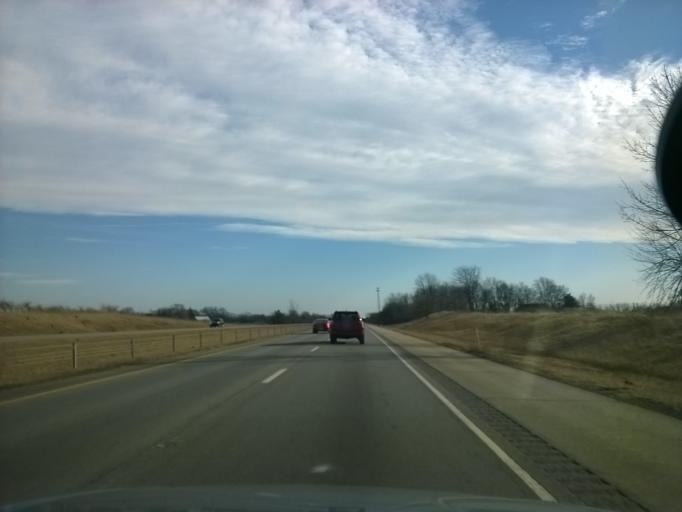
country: US
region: Indiana
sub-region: Johnson County
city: Edinburgh
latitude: 39.4308
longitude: -85.9773
